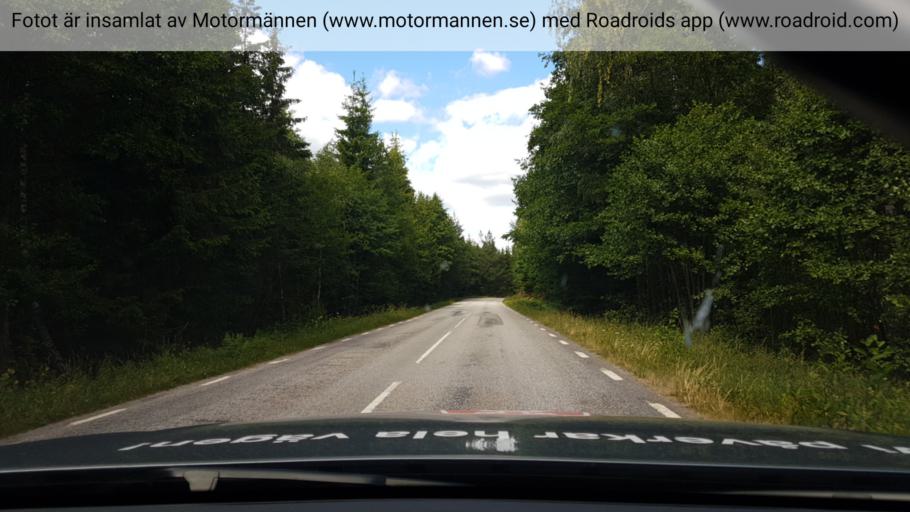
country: SE
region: Kalmar
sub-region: Vasterviks Kommun
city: Forserum
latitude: 58.0231
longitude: 16.5322
